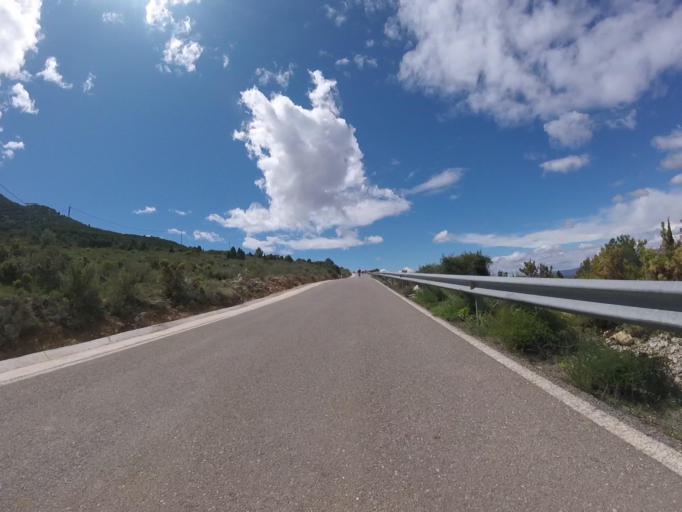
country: ES
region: Valencia
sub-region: Provincia de Castello
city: Sierra-Engarceran
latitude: 40.2933
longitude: -0.0366
